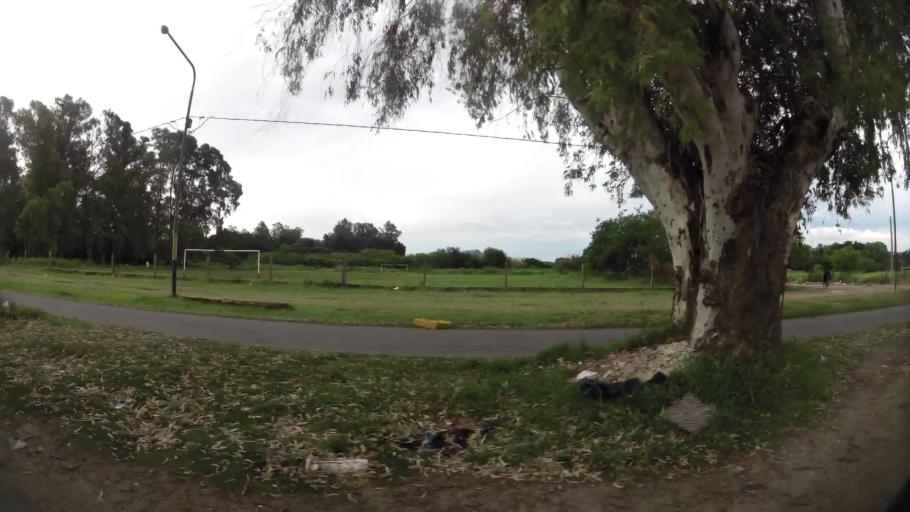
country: AR
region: Santa Fe
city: Gobernador Galvez
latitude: -32.9983
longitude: -60.6844
